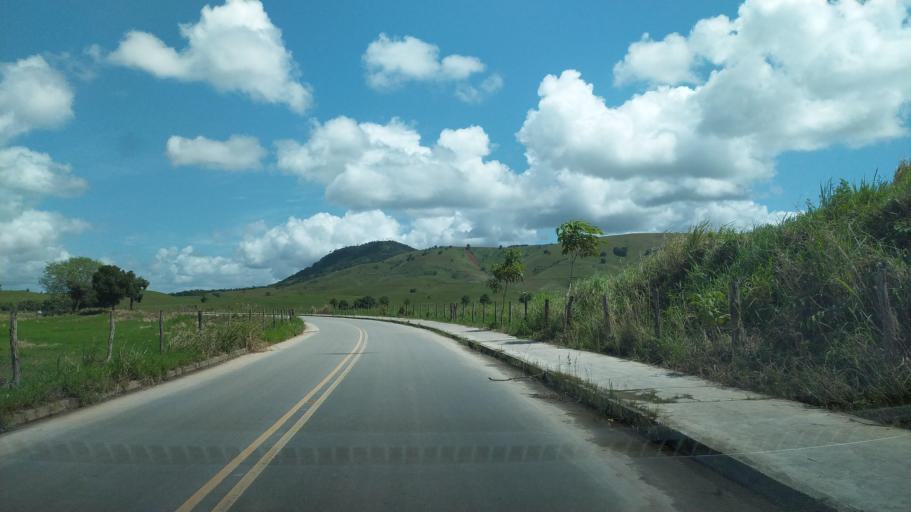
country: BR
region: Alagoas
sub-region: Uniao Dos Palmares
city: Uniao dos Palmares
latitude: -9.1573
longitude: -36.0428
